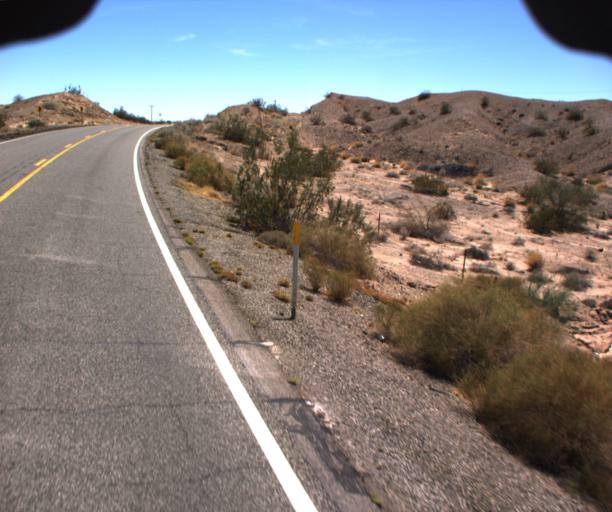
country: US
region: Arizona
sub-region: La Paz County
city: Parker
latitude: 34.0119
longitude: -114.2438
